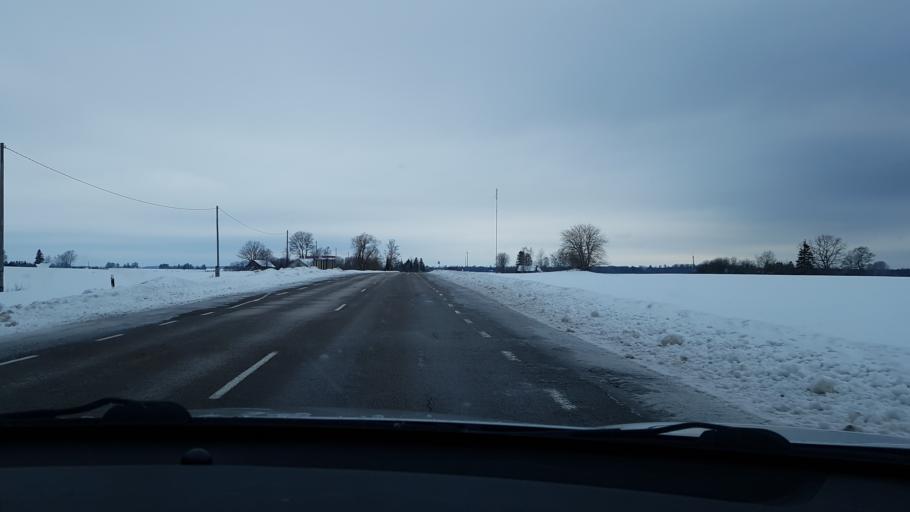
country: EE
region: Jaervamaa
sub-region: Jaerva-Jaani vald
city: Jarva-Jaani
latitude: 58.9178
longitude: 25.8726
